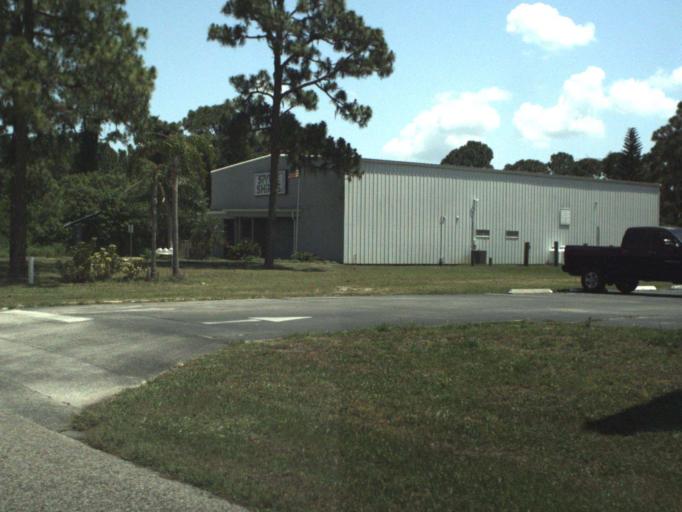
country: US
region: Florida
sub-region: Brevard County
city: Sharpes
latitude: 28.4681
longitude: -80.7097
